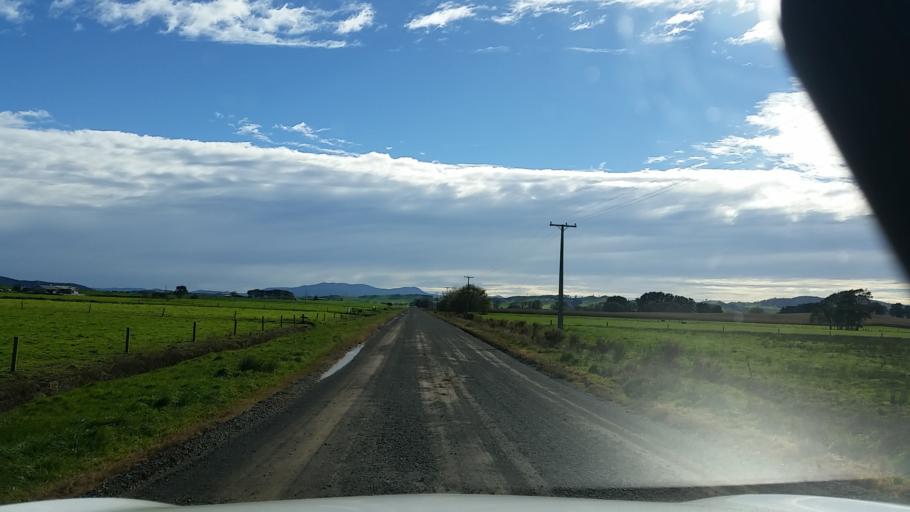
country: NZ
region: Waikato
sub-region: Hamilton City
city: Hamilton
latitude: -37.6373
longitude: 175.4300
